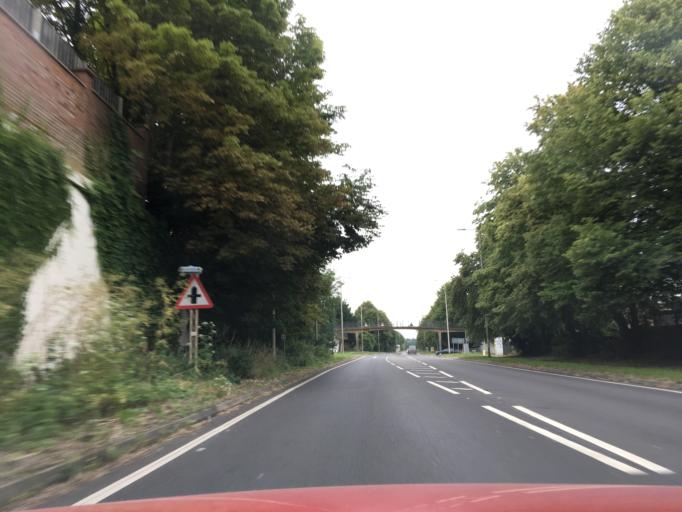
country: GB
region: England
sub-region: Hertfordshire
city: Markyate
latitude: 51.8371
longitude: -0.4585
